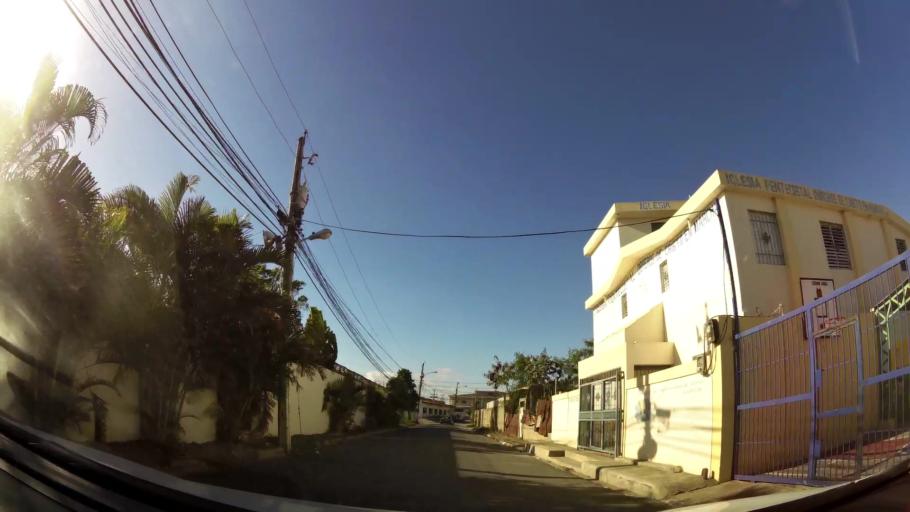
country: DO
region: Santo Domingo
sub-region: Santo Domingo
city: Santo Domingo Este
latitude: 18.4913
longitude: -69.8132
